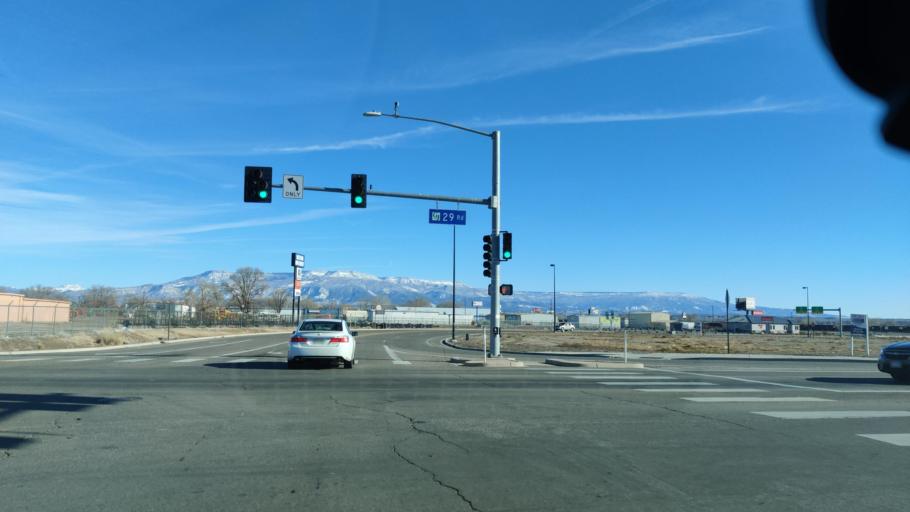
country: US
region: Colorado
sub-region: Mesa County
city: Fruitvale
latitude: 39.0753
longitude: -108.5153
